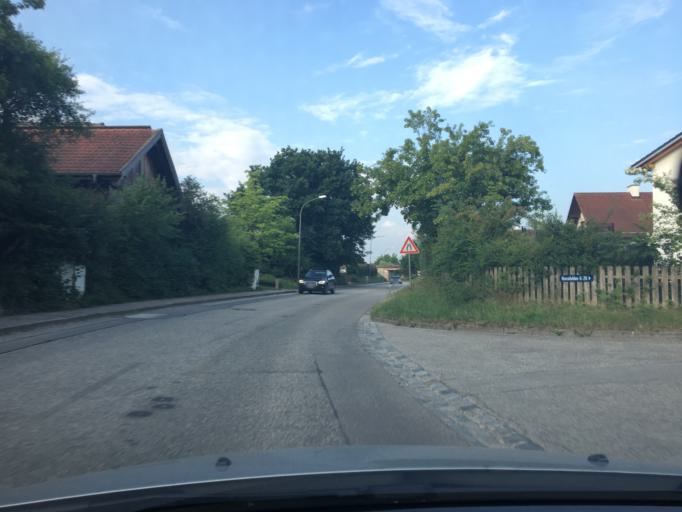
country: DE
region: Bavaria
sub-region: Lower Bavaria
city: Vilsbiburg
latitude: 48.4437
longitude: 12.3481
